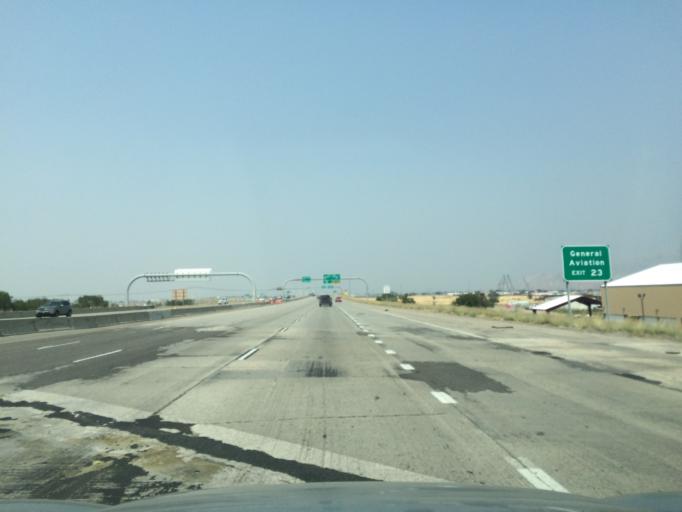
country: US
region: Utah
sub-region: Salt Lake County
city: Salt Lake City
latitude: 40.7471
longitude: -111.9486
